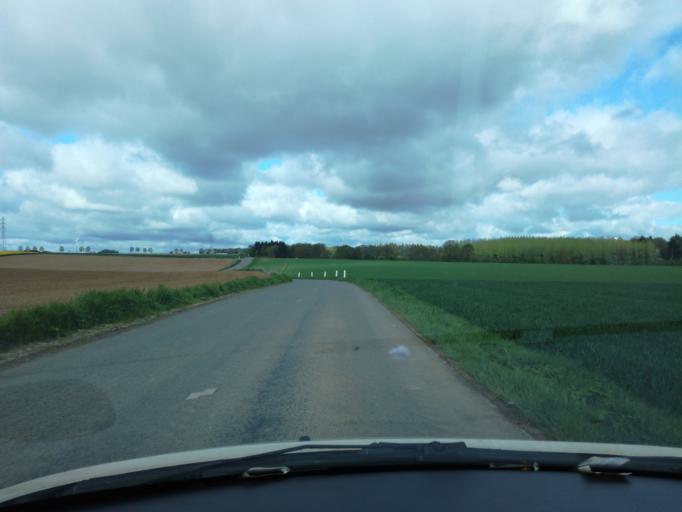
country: FR
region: Picardie
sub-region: Departement de la Somme
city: Poix-de-Picardie
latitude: 49.8162
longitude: 1.9897
